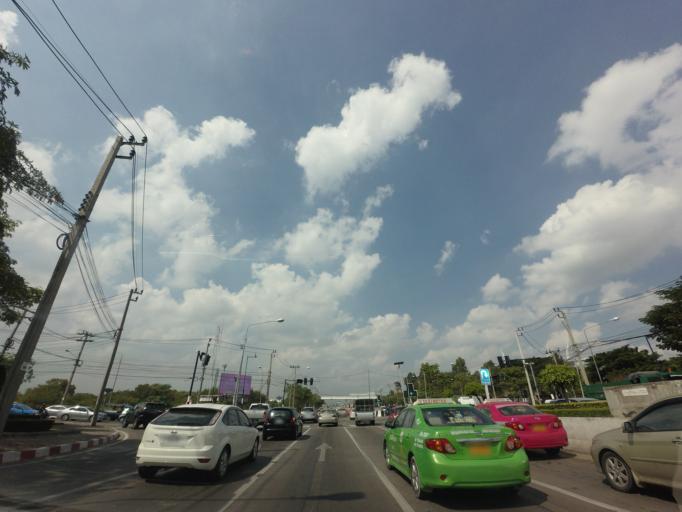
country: TH
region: Bangkok
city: Lat Phrao
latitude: 13.8325
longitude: 100.6115
